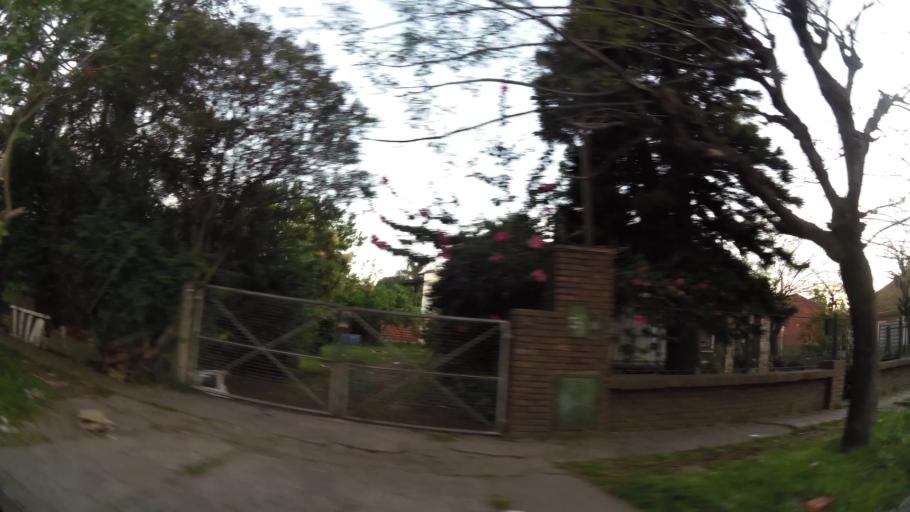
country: AR
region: Buenos Aires
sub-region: Partido de Quilmes
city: Quilmes
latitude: -34.7773
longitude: -58.2119
